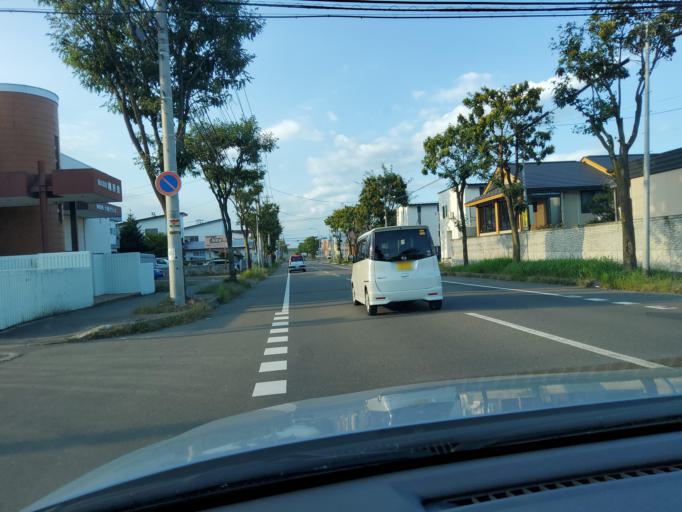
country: JP
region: Hokkaido
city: Obihiro
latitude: 42.9345
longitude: 143.1845
